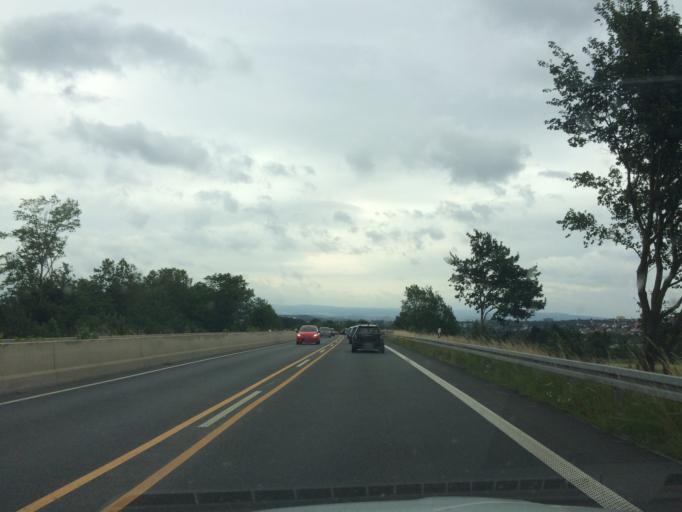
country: DE
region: Hesse
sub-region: Regierungsbezirk Kassel
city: Espenau
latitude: 51.3728
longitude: 9.4474
